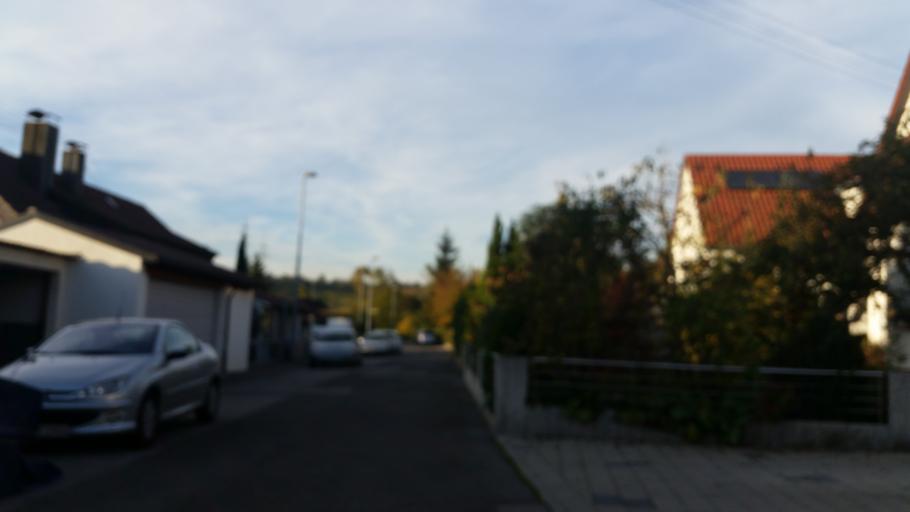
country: DE
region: Baden-Wuerttemberg
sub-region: Regierungsbezirk Stuttgart
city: Freiberg am Neckar
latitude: 48.9160
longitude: 9.2159
